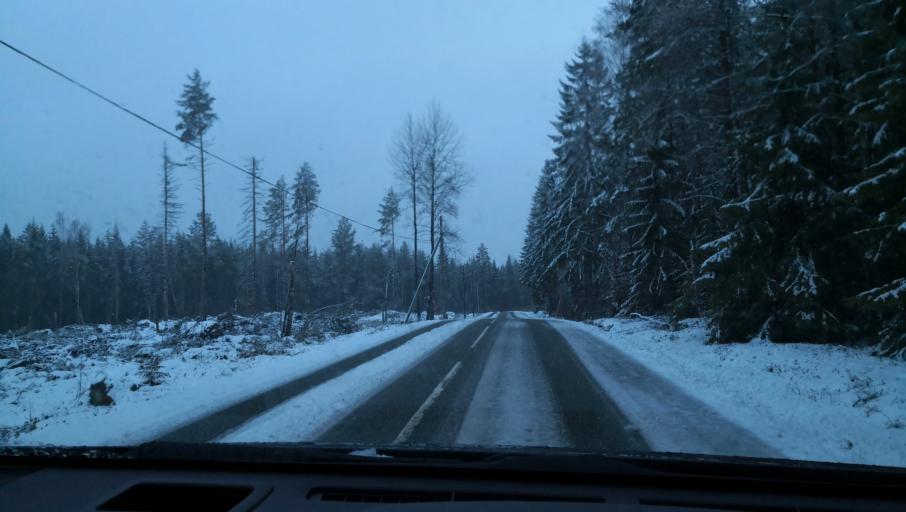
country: SE
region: Vaestmanland
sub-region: Kopings Kommun
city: Kolsva
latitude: 59.5855
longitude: 15.8052
